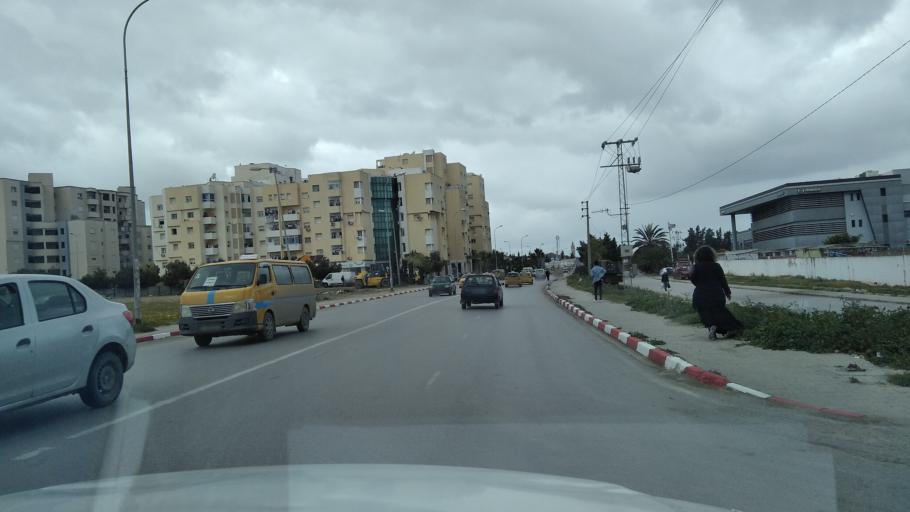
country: TN
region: Bin 'Arus
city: Ben Arous
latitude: 36.7471
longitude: 10.2311
